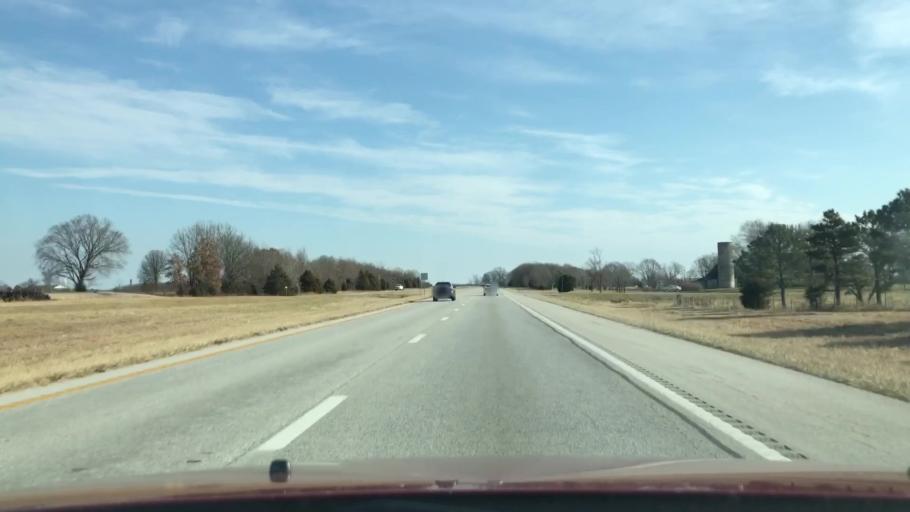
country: US
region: Missouri
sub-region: Webster County
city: Rogersville
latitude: 37.1237
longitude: -92.9893
